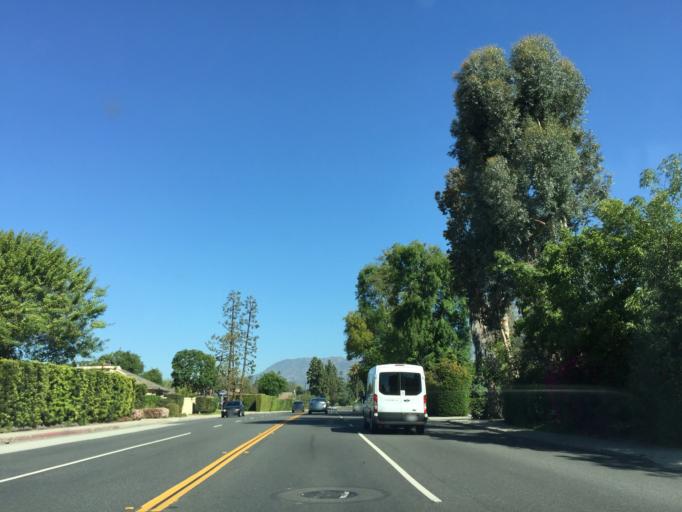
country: US
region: California
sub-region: Los Angeles County
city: East Pasadena
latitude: 34.1299
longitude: -118.0924
